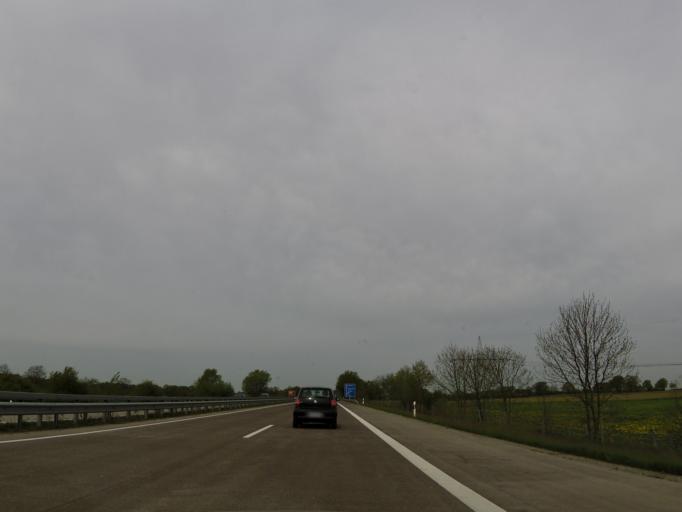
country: DE
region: Schleswig-Holstein
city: Hohenfelde
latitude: 53.8369
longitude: 9.6154
